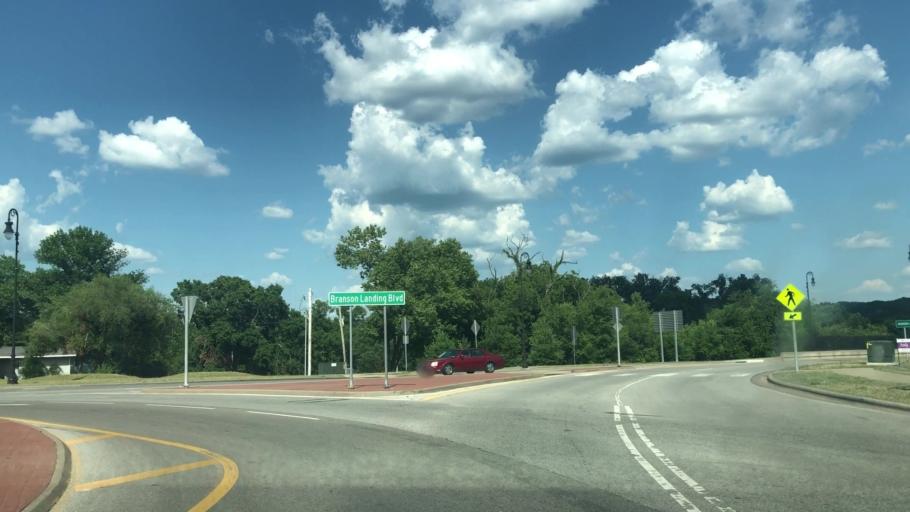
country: US
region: Missouri
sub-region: Taney County
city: Branson
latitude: 36.6495
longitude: -93.2195
